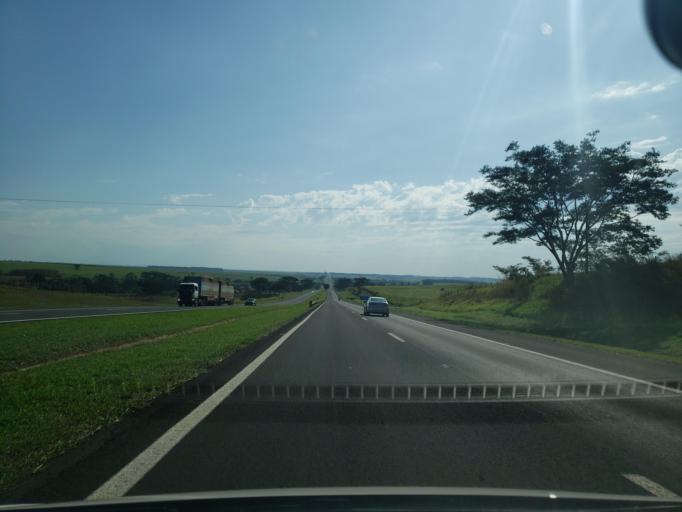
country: BR
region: Sao Paulo
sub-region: Penapolis
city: Penapolis
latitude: -21.5062
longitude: -50.0253
